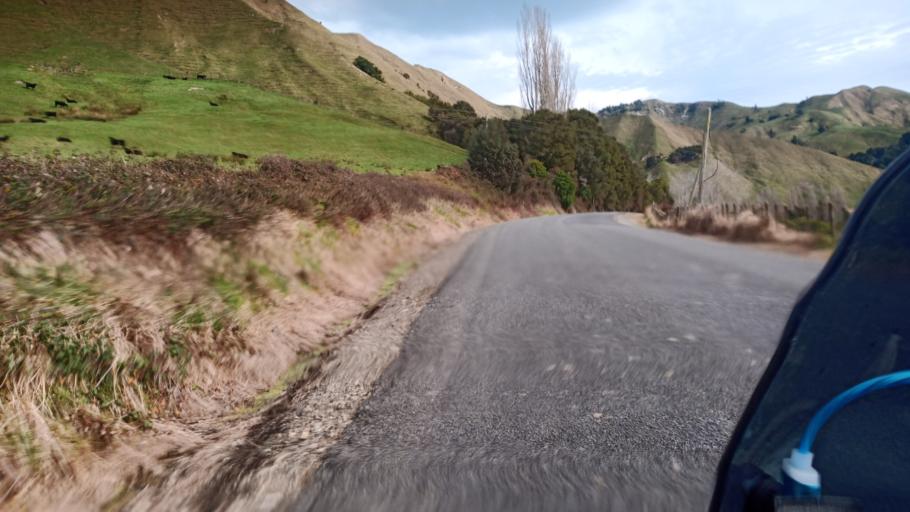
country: NZ
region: Hawke's Bay
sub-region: Wairoa District
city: Wairoa
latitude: -38.7954
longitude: 177.4446
